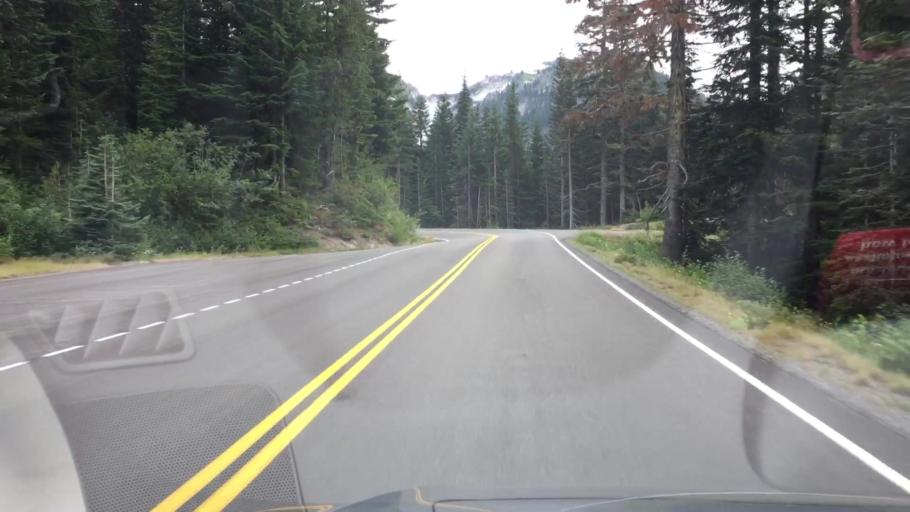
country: US
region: Washington
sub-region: Pierce County
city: Buckley
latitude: 46.7767
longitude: -121.7574
